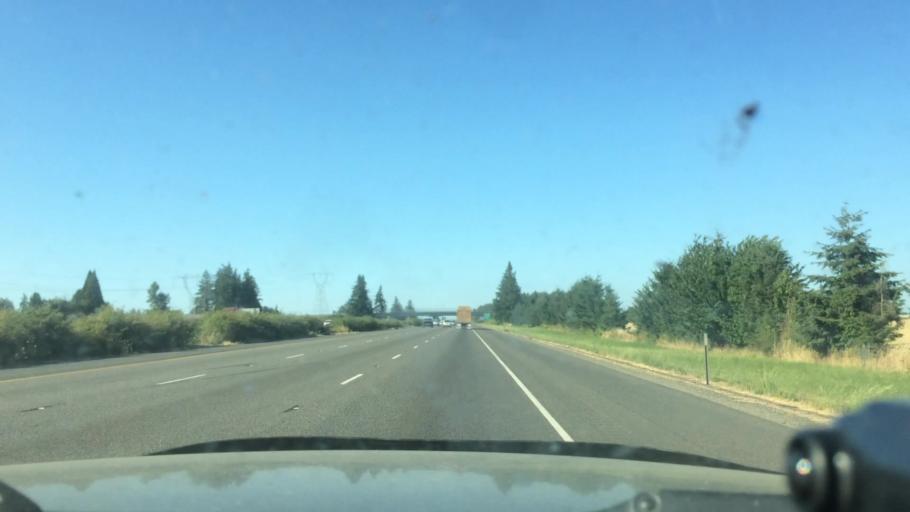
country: US
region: Oregon
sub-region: Marion County
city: Hayesville
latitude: 45.0304
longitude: -122.9829
